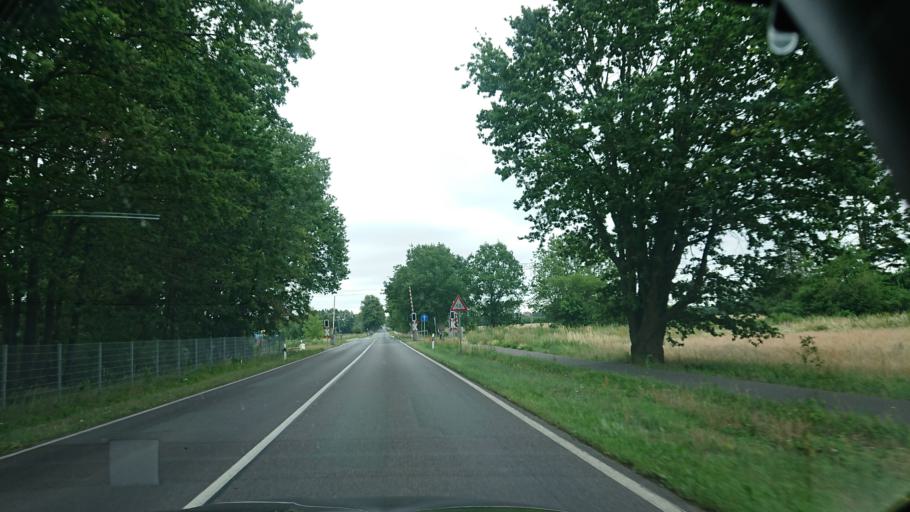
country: DE
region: Brandenburg
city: Perleberg
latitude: 53.0682
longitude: 11.8822
